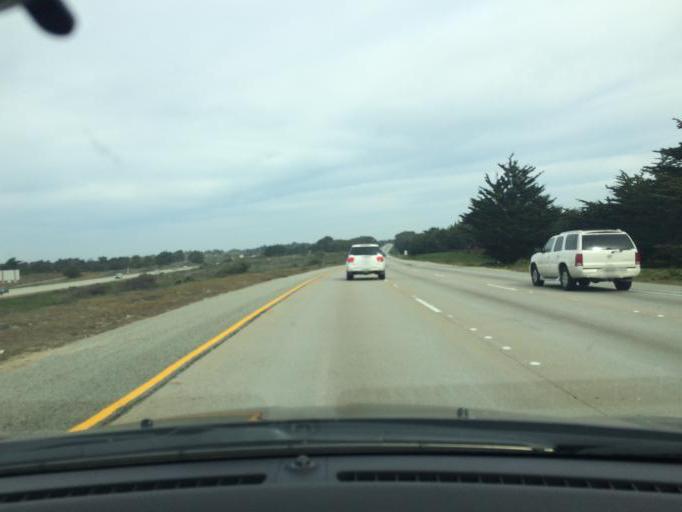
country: US
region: California
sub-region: Monterey County
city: Seaside
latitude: 36.6373
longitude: -121.8295
